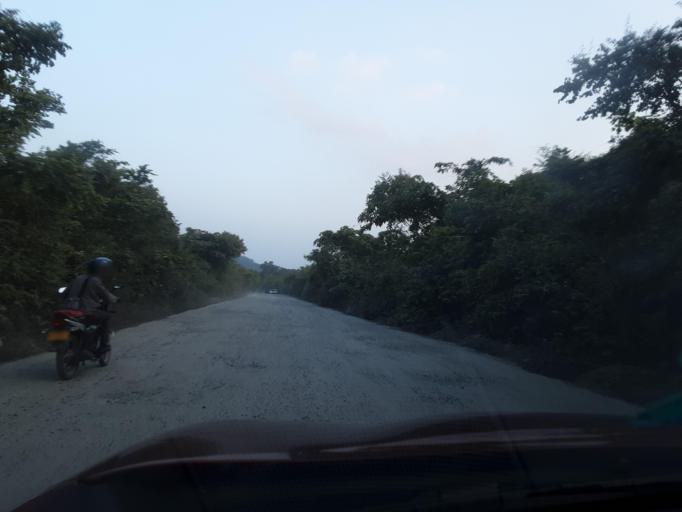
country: LK
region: Central
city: Dambulla
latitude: 7.8078
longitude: 80.7815
